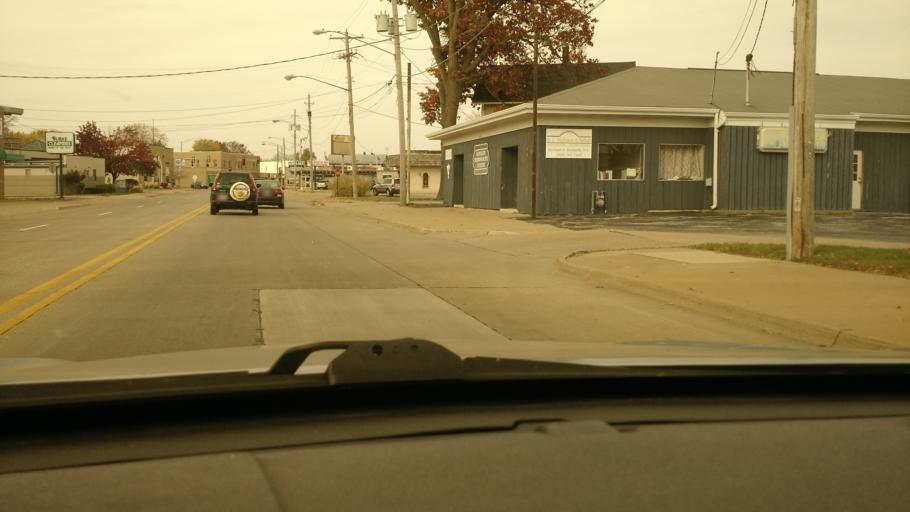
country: US
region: Illinois
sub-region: Rock Island County
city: Moline
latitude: 41.4952
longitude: -90.5147
